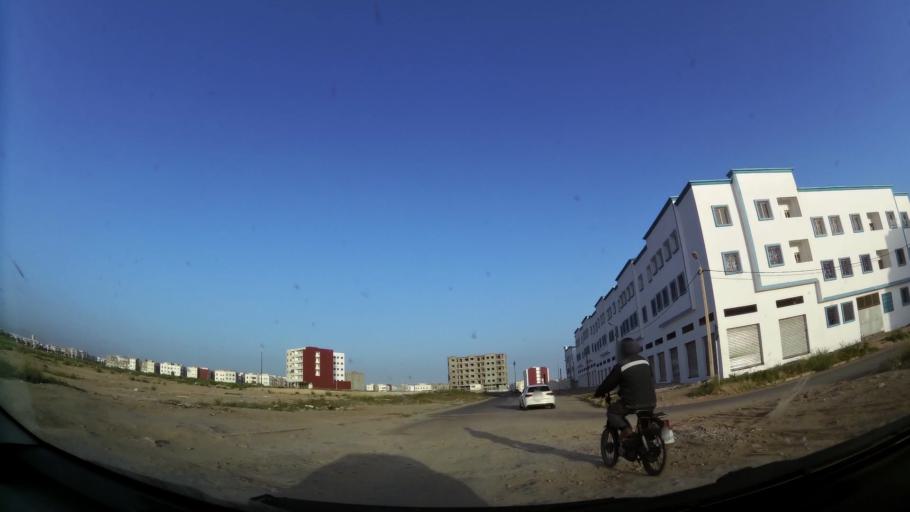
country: MA
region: Oued ed Dahab-Lagouira
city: Dakhla
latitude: 30.4006
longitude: -9.5673
